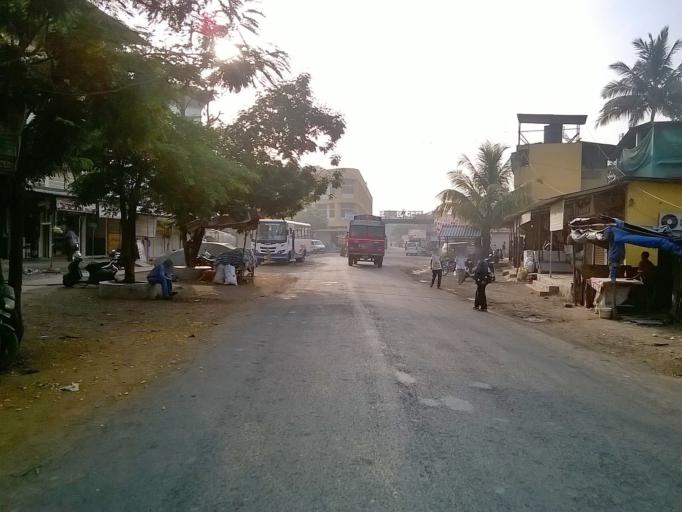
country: IN
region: Maharashtra
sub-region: Raigarh
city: Kalundri
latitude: 19.0134
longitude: 73.1696
